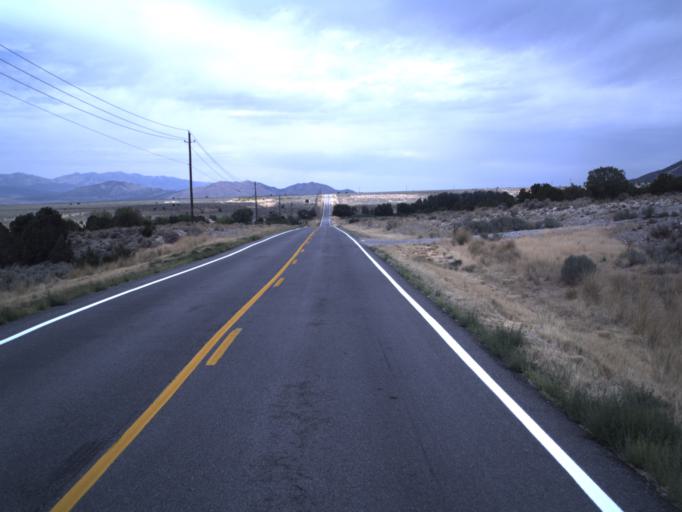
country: US
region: Utah
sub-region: Tooele County
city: Tooele
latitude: 40.3368
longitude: -112.2999
